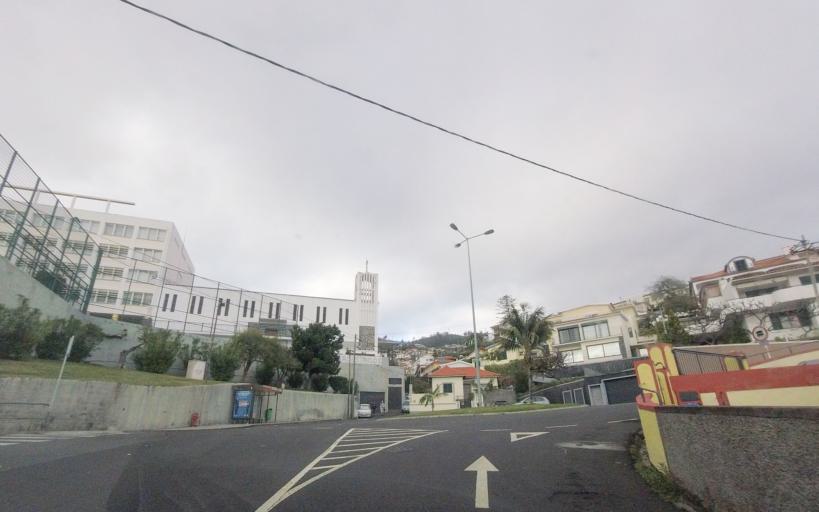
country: PT
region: Madeira
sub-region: Funchal
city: Nossa Senhora do Monte
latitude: 32.6560
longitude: -16.8968
